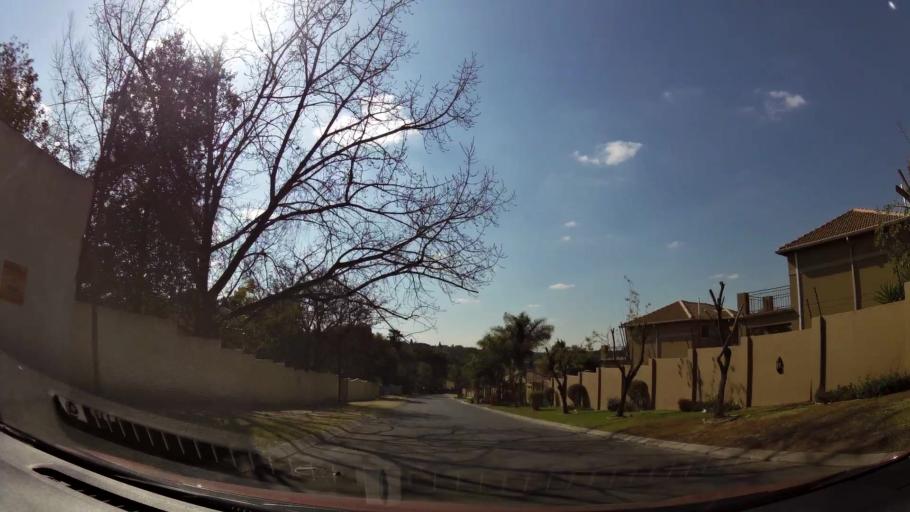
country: ZA
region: Gauteng
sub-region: City of Johannesburg Metropolitan Municipality
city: Roodepoort
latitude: -26.0769
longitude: 27.9417
